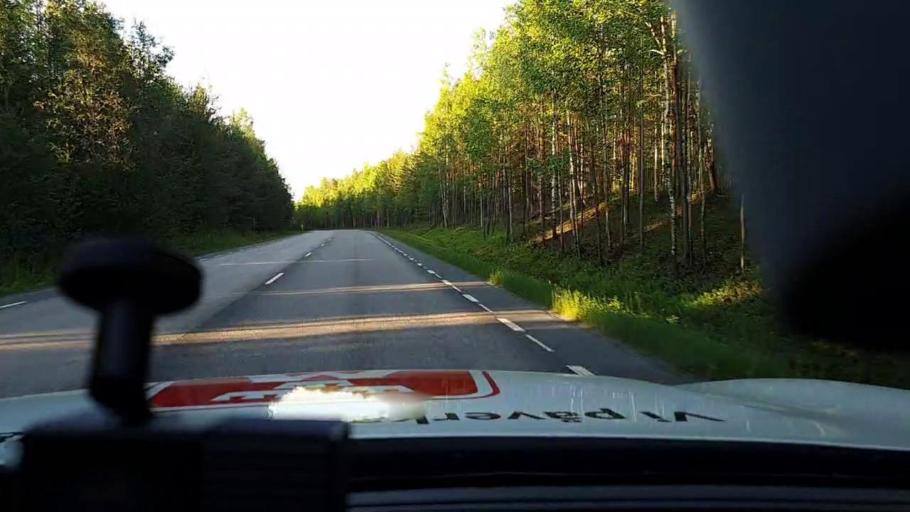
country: SE
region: Norrbotten
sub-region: Lulea Kommun
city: Lulea
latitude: 65.6143
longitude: 22.1954
